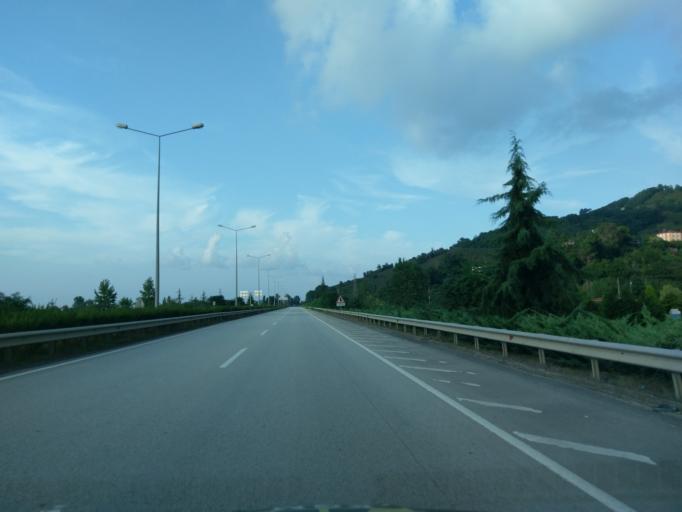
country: TR
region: Ordu
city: Ordu
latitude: 41.0058
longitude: 37.8279
